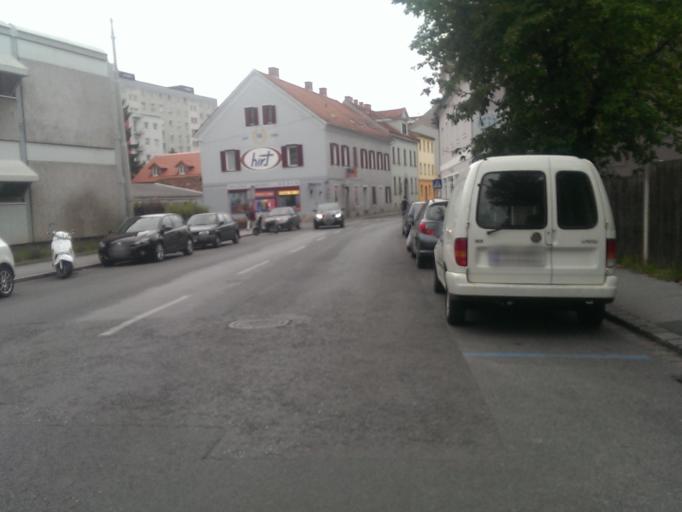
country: AT
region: Styria
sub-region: Graz Stadt
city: Graz
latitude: 47.0634
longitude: 15.4561
